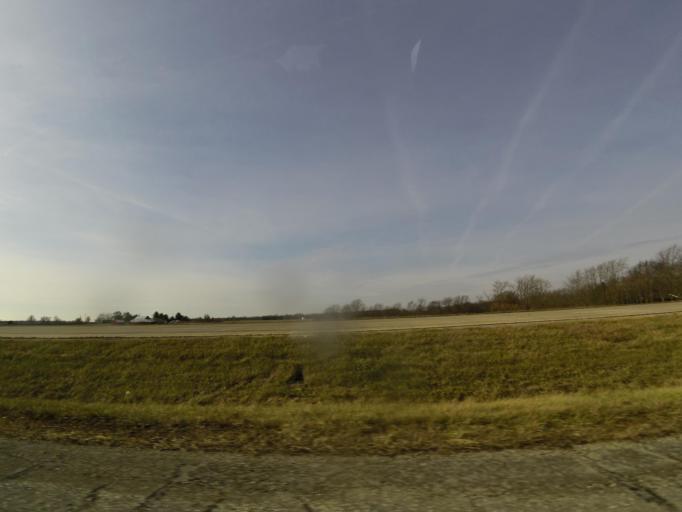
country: US
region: Illinois
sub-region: De Witt County
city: Clinton
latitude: 40.1493
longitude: -88.9855
